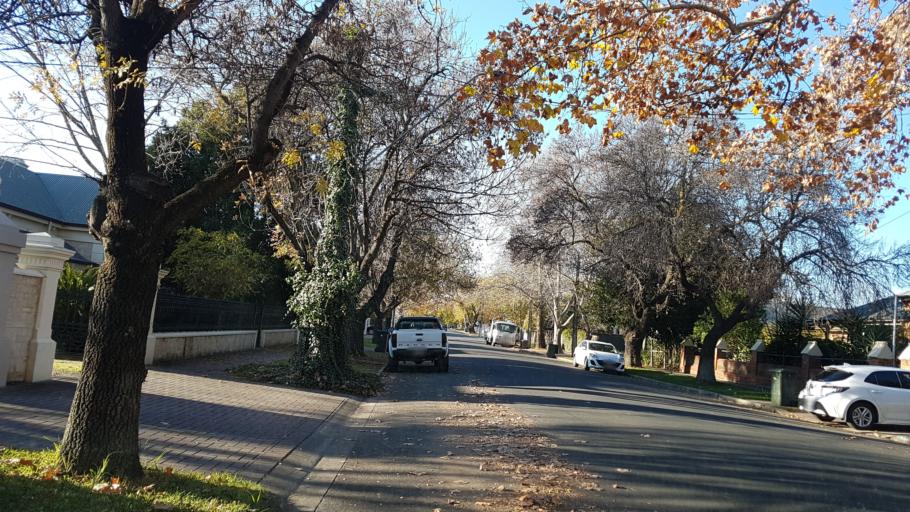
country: AU
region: South Australia
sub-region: Norwood Payneham St Peters
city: Royston Park
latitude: -34.9058
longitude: 138.6229
